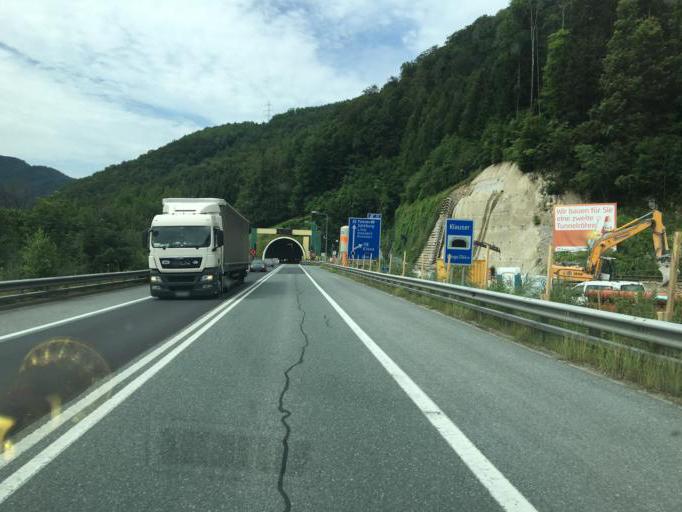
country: AT
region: Upper Austria
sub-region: Politischer Bezirk Kirchdorf an der Krems
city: Micheldorf in Oberoesterreich
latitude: 47.8188
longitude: 14.1687
